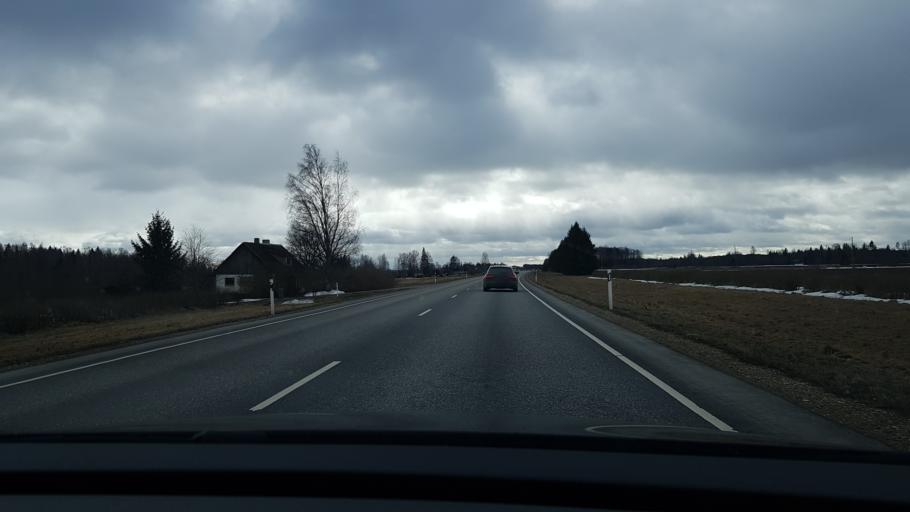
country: EE
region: Paernumaa
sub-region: Vaendra vald (alev)
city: Vandra
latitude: 58.6098
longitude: 24.9180
